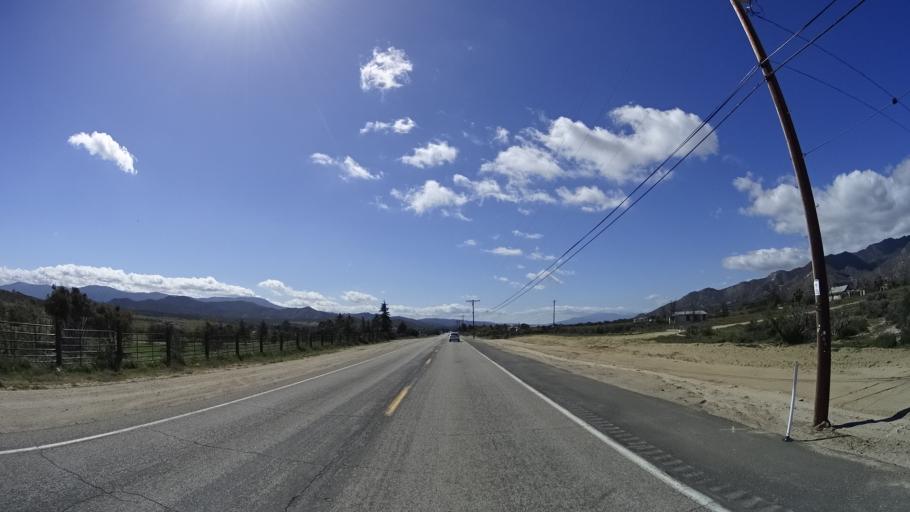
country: US
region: California
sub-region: San Diego County
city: Borrego Springs
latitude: 33.2103
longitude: -116.5152
